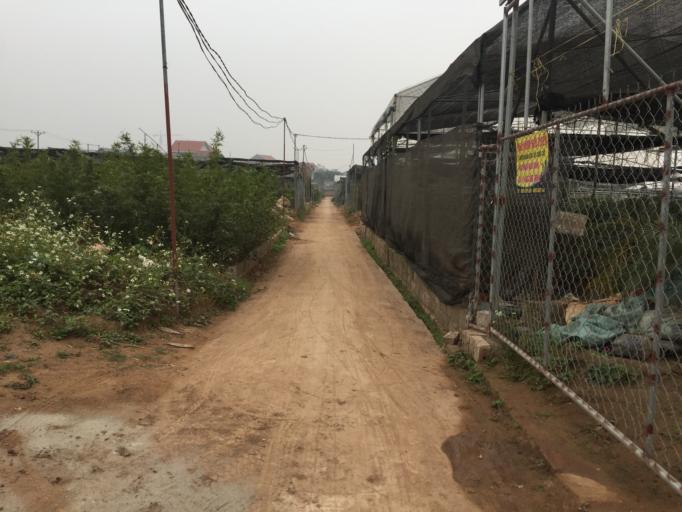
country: VN
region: Hung Yen
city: Van Giang
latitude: 20.9649
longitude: 105.9105
